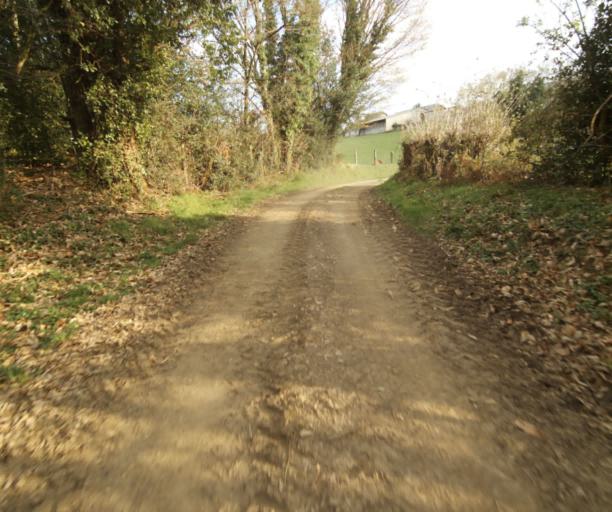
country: FR
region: Limousin
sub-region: Departement de la Correze
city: Saint-Clement
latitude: 45.3671
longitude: 1.6314
